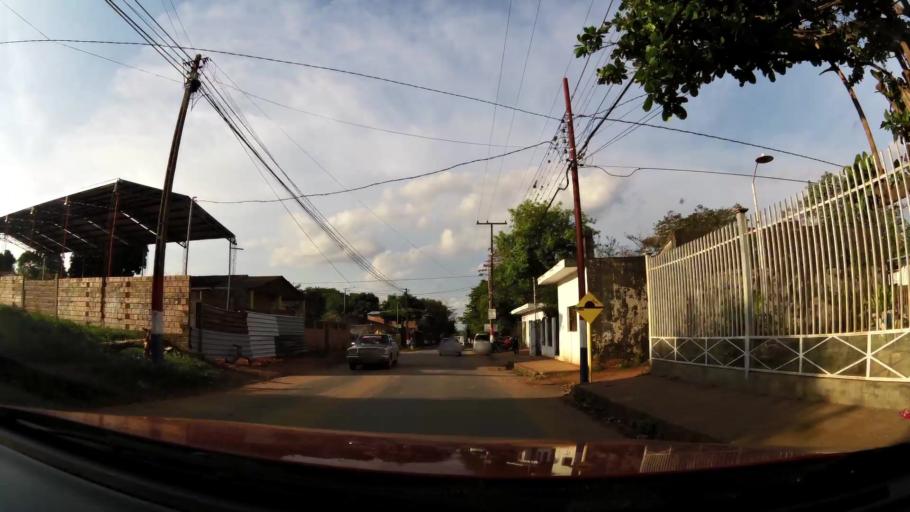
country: PY
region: Central
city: Fernando de la Mora
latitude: -25.3600
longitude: -57.5293
